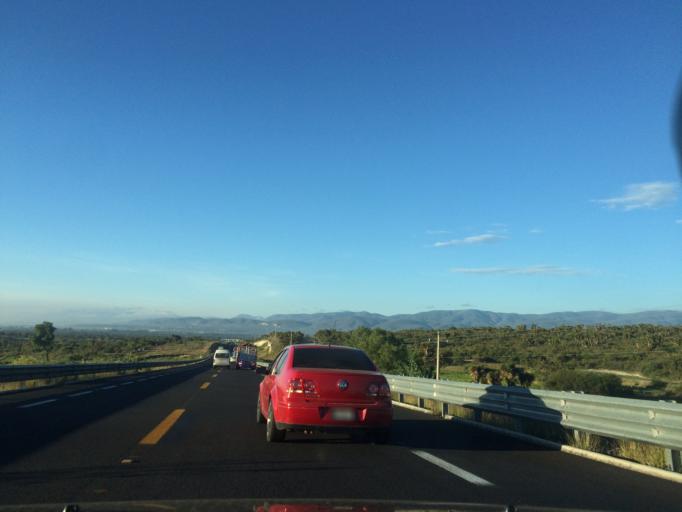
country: MX
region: Puebla
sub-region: Tehuacan
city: Magdalena Cuayucatepec
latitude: 18.5668
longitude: -97.4639
